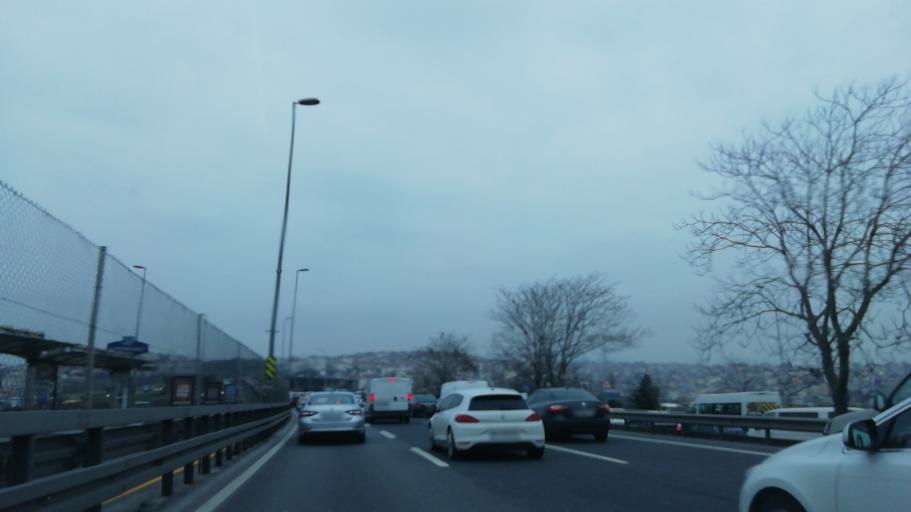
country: TR
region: Istanbul
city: Istanbul
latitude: 41.0390
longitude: 28.9380
